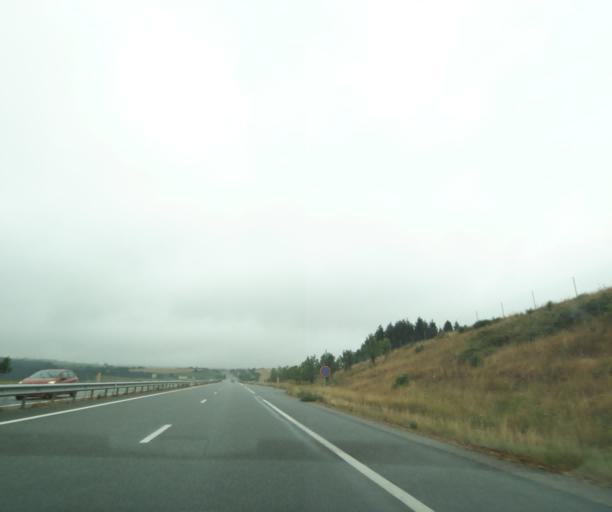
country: FR
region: Midi-Pyrenees
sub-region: Departement de l'Aveyron
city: Naucelle
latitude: 44.1146
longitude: 2.3122
